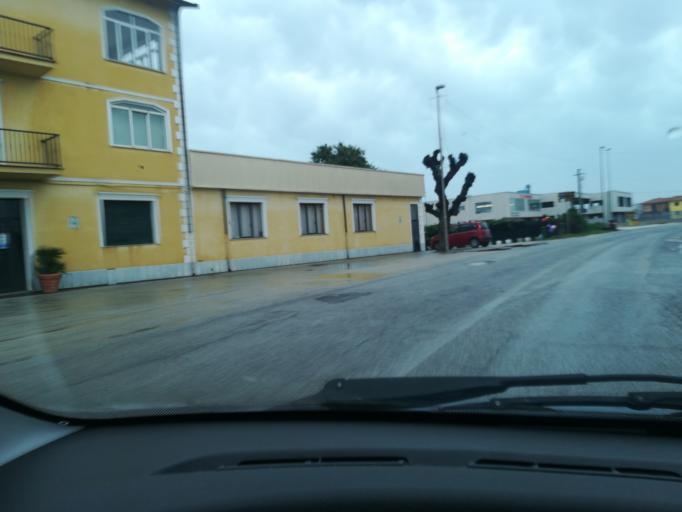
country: IT
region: The Marches
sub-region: Provincia di Macerata
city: Trodica
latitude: 43.2762
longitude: 13.6015
